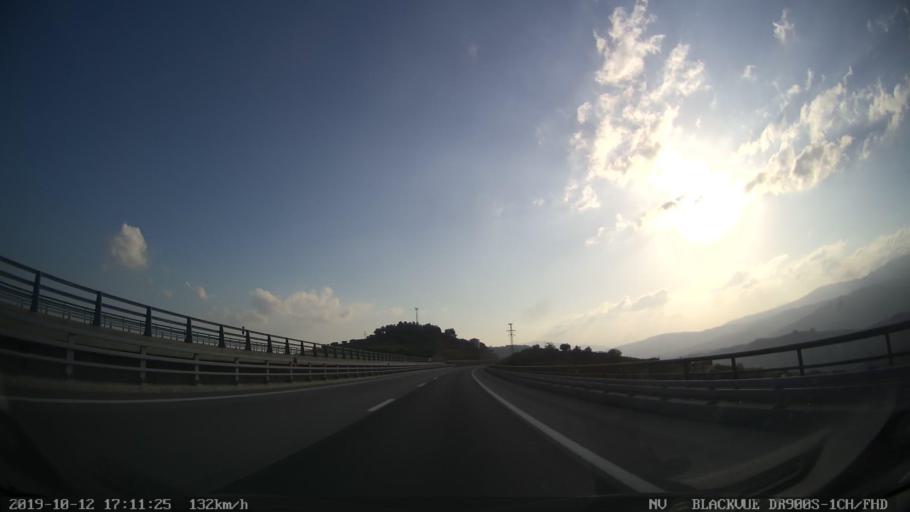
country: PT
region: Vila Real
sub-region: Vila Real
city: Vila Real
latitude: 41.2379
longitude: -7.7279
